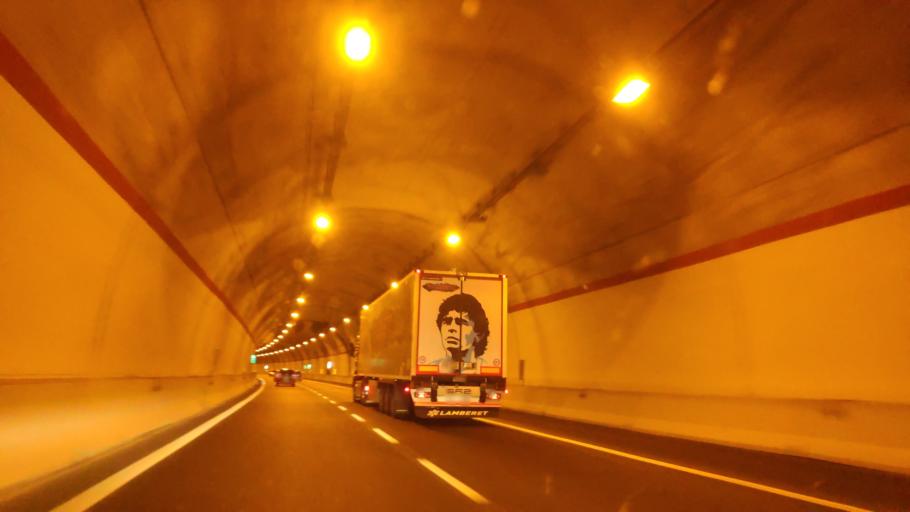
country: IT
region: Basilicate
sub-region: Provincia di Potenza
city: Lauria
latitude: 40.0397
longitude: 15.8720
